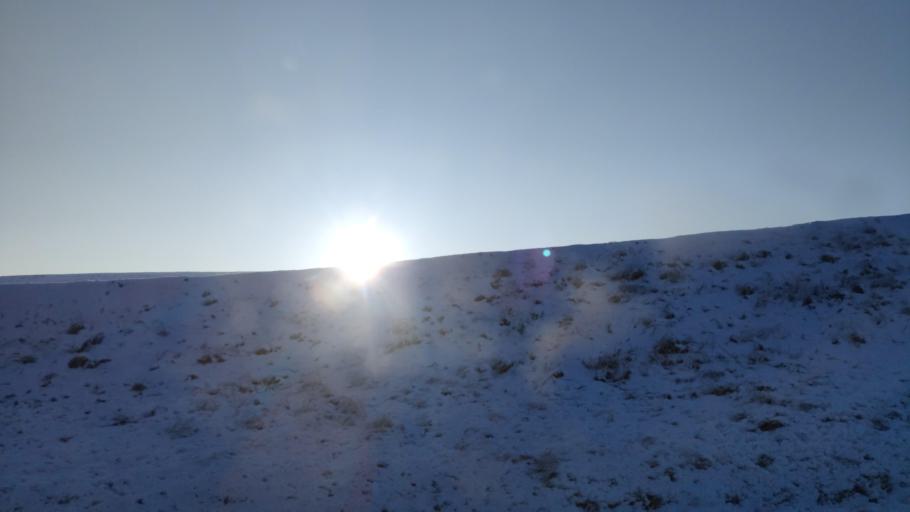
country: PL
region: Kujawsko-Pomorskie
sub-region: Powiat zninski
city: Barcin
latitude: 52.8725
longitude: 17.8507
